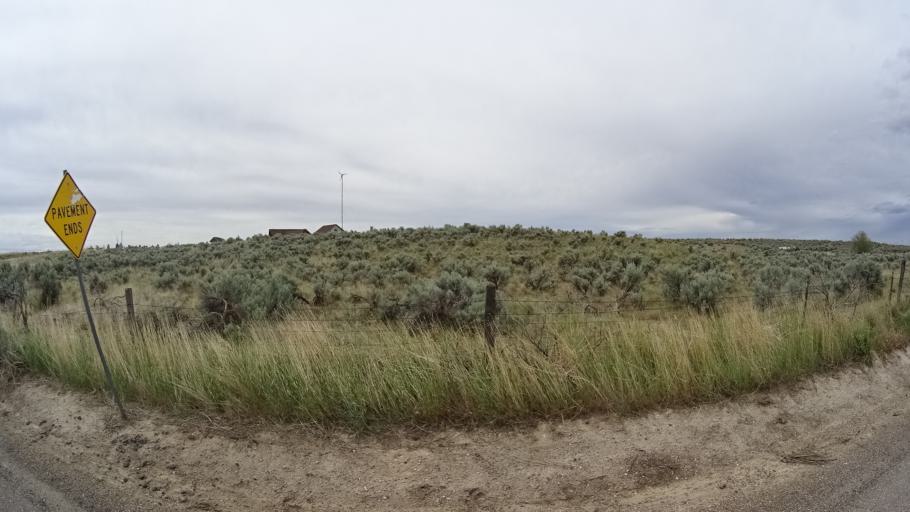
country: US
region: Idaho
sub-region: Ada County
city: Boise
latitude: 43.3888
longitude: -115.9739
